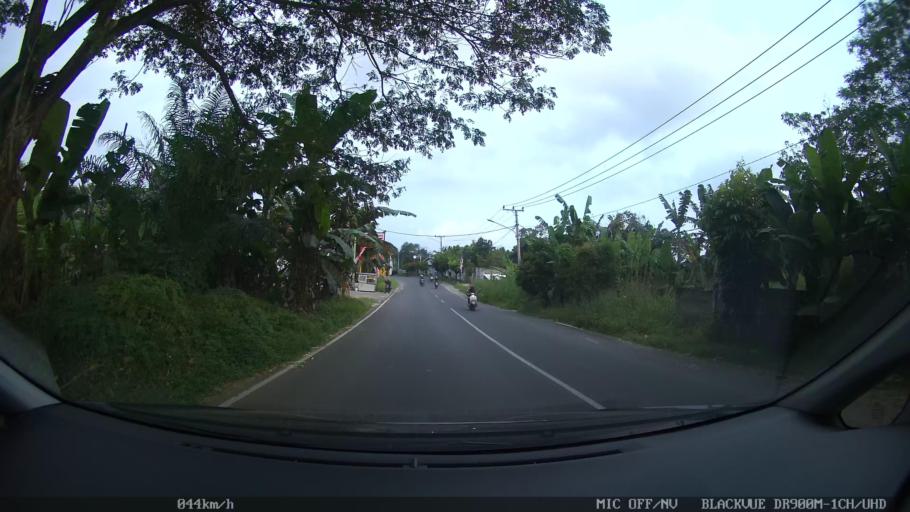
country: ID
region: Lampung
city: Bandarlampung
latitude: -5.4294
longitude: 105.2366
